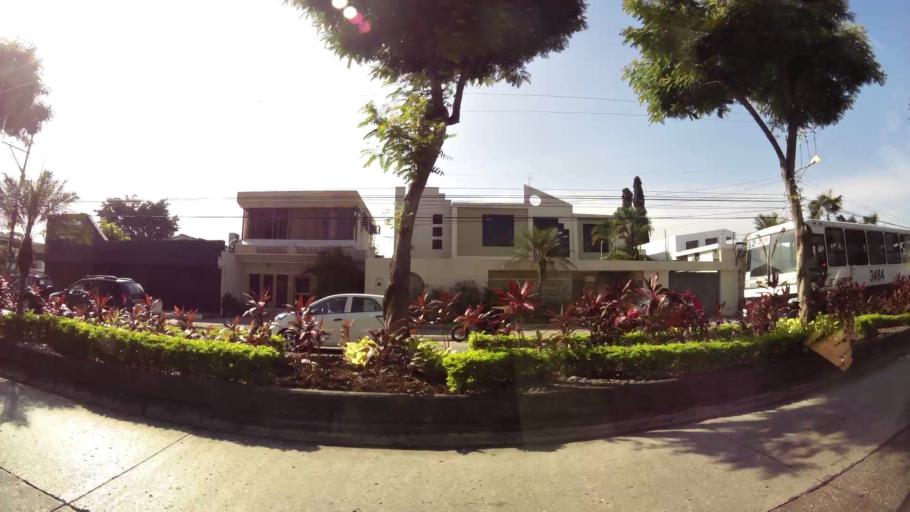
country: EC
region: Guayas
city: Guayaquil
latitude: -2.1688
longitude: -79.9052
